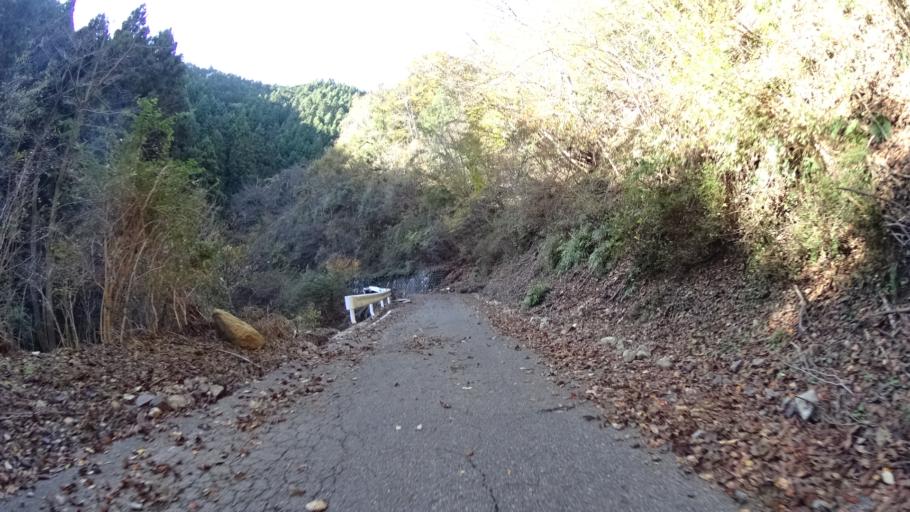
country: JP
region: Kanagawa
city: Atsugi
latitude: 35.5096
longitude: 139.2674
